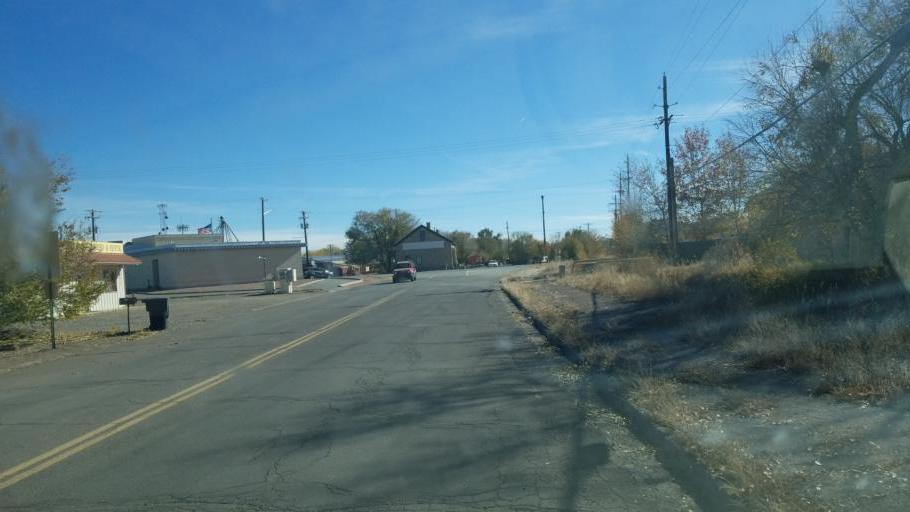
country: US
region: Colorado
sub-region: Rio Grande County
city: Monte Vista
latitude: 37.5817
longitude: -106.1507
